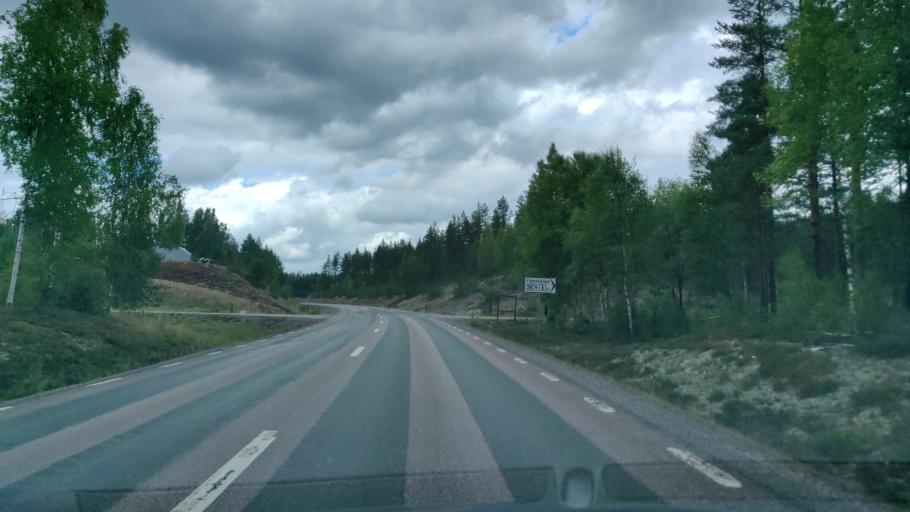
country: SE
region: Vaermland
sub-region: Torsby Kommun
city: Torsby
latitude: 60.5280
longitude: 13.1306
